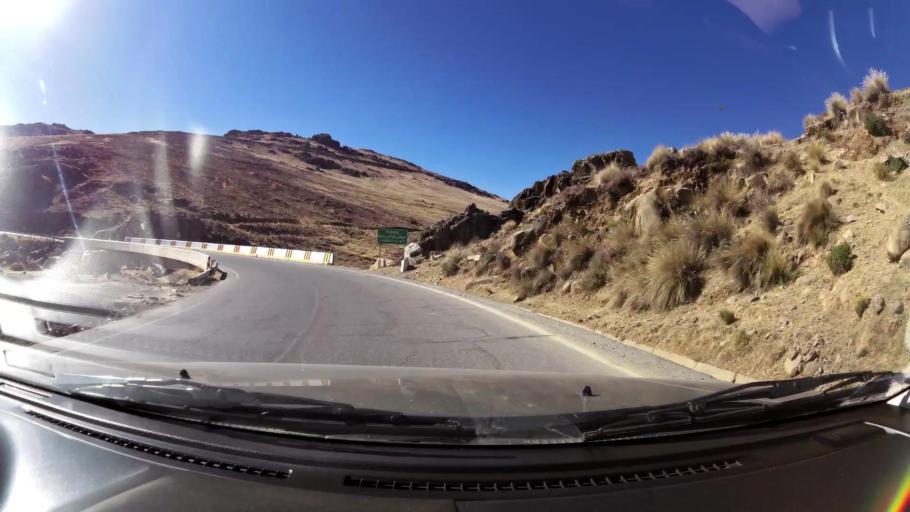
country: PE
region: Huancavelica
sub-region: Huaytara
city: Huayacundo Arma
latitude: -13.5637
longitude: -75.2316
